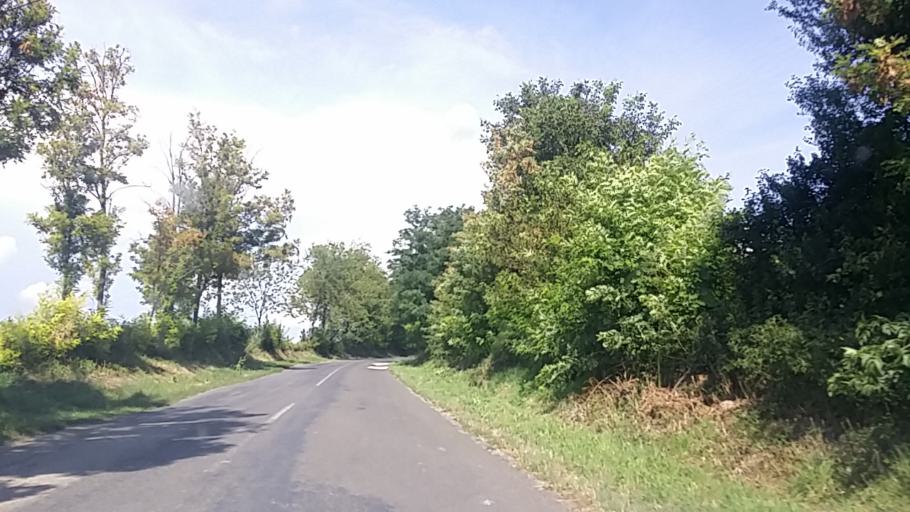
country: HU
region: Tolna
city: Hogyesz
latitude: 46.5193
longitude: 18.4081
